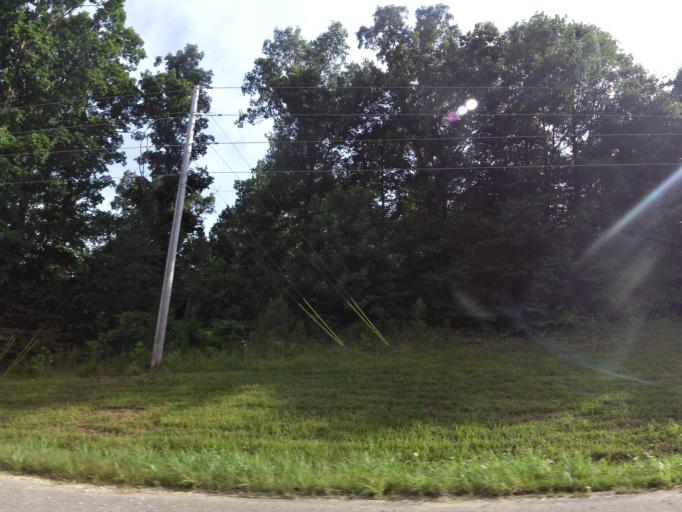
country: US
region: Tennessee
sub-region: Benton County
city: Camden
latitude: 36.0415
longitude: -88.1361
